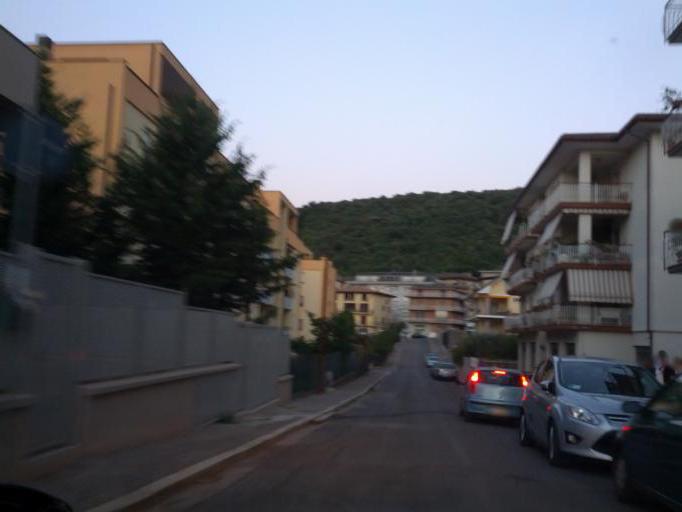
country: IT
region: Latium
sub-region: Provincia di Latina
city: Itri
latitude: 41.2879
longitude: 13.5235
